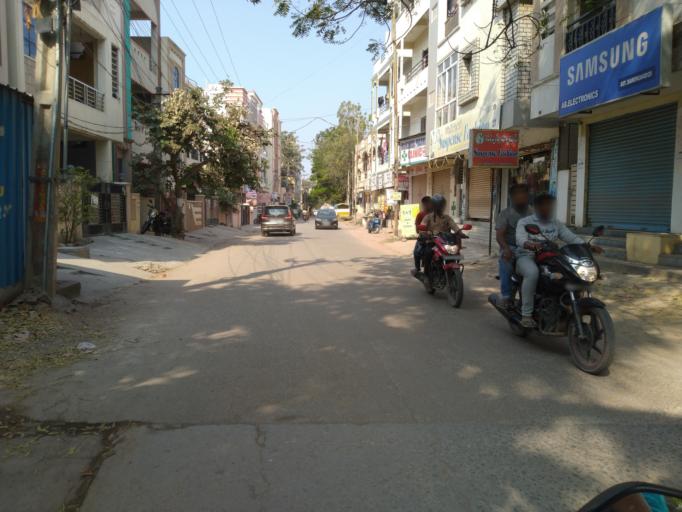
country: IN
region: Telangana
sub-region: Rangareddi
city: Quthbullapur
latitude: 17.4991
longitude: 78.4705
